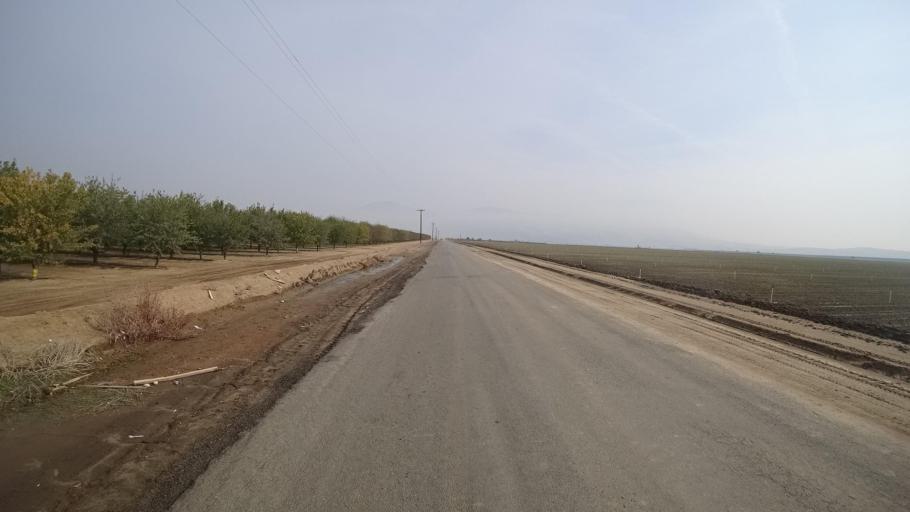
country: US
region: California
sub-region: Kern County
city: Arvin
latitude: 35.1798
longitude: -118.8649
